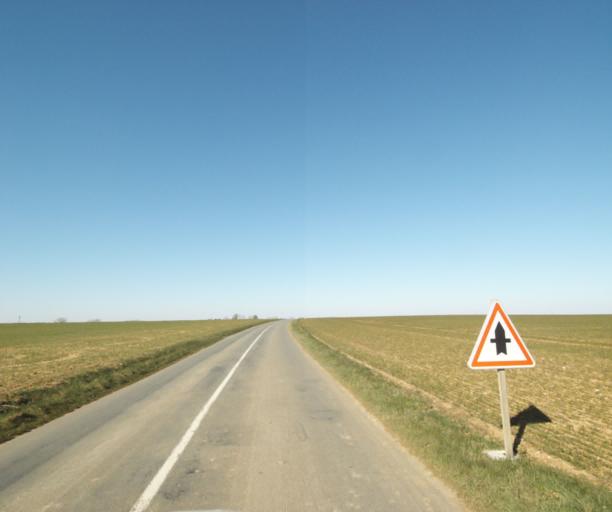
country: FR
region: Poitou-Charentes
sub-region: Departement des Deux-Sevres
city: Saint-Maxire
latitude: 46.3679
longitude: -0.4917
